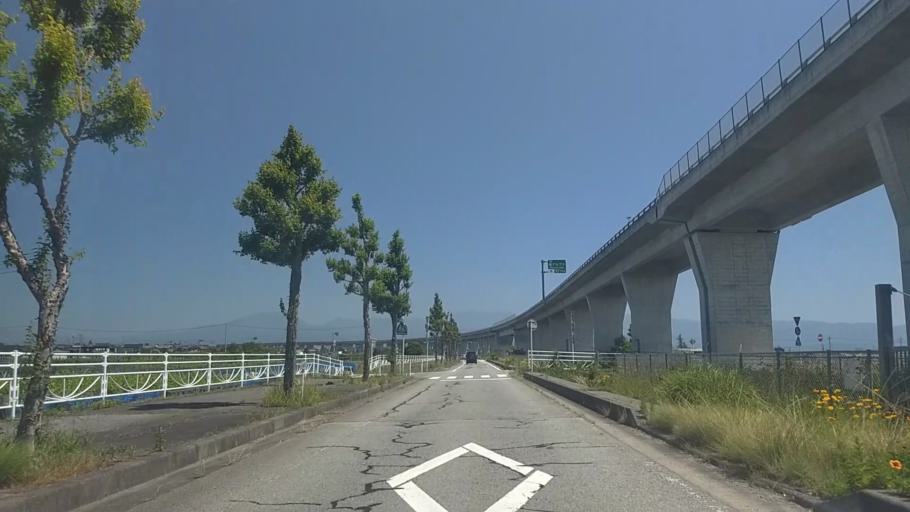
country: JP
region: Yamanashi
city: Ryuo
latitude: 35.6028
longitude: 138.4797
